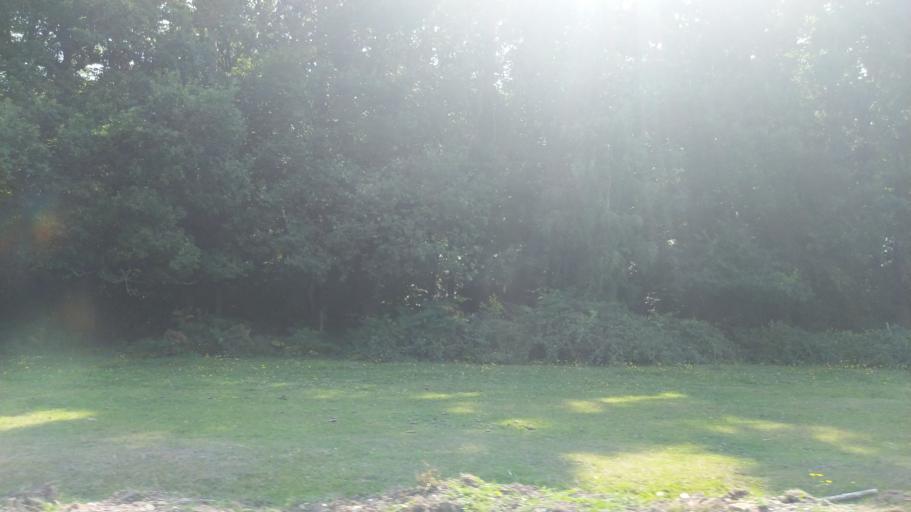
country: GB
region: England
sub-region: Hampshire
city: Lyndhurst
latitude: 50.8981
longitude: -1.5391
